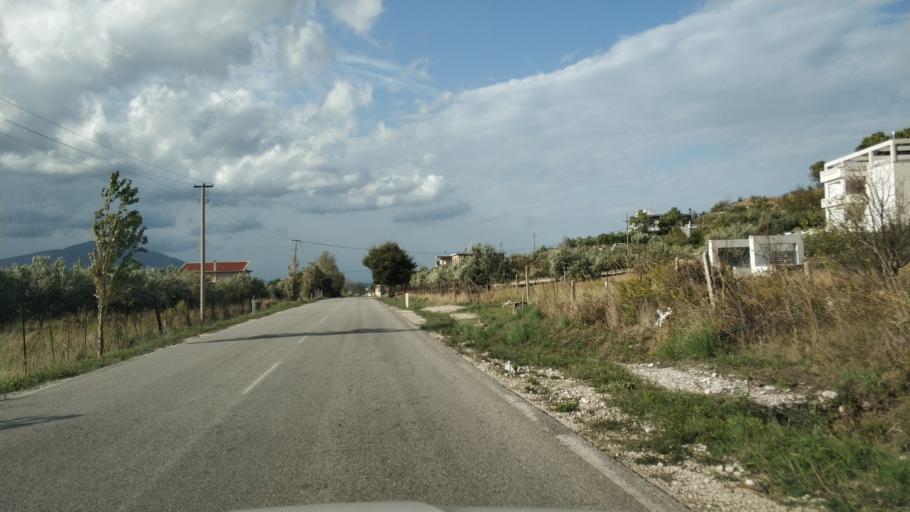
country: AL
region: Vlore
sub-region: Rrethi i Vlores
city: Orikum
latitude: 40.3015
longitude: 19.4849
